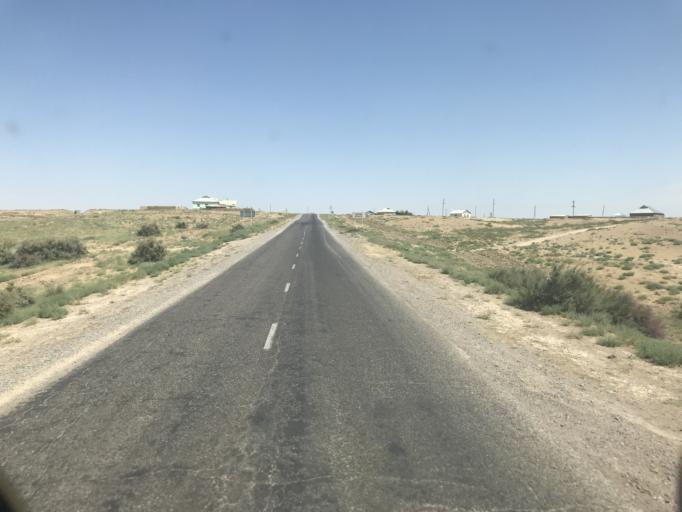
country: UZ
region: Toshkent
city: Chinoz
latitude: 41.2153
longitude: 68.5999
